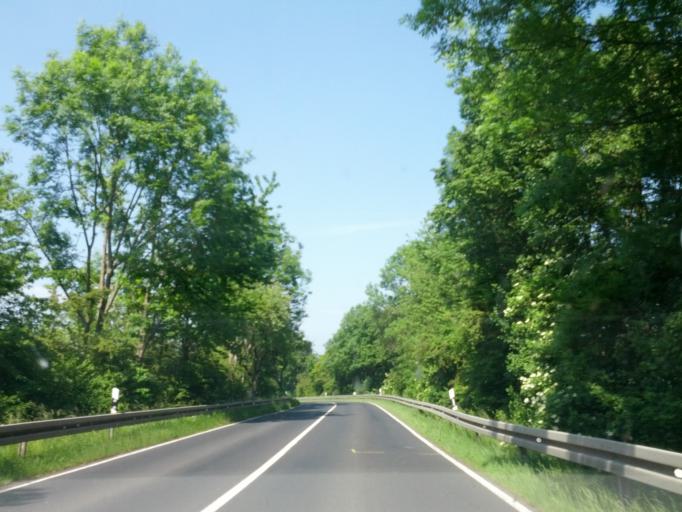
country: DE
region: Thuringia
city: Empfertshausen
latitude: 50.6698
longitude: 10.1150
